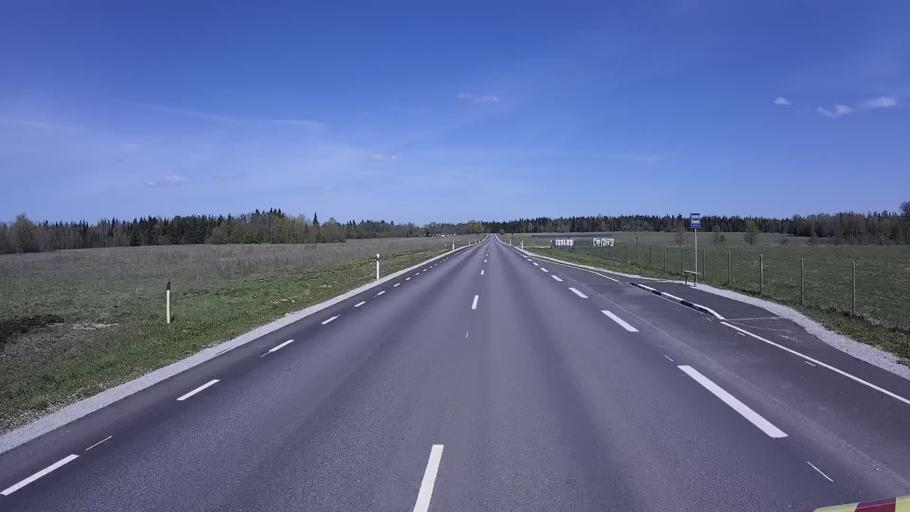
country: EE
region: Harju
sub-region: Paldiski linn
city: Paldiski
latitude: 59.1921
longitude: 24.0924
